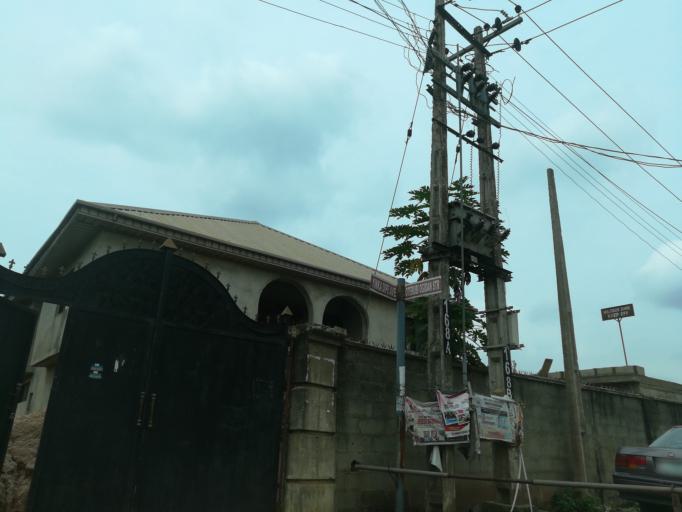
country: NG
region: Lagos
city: Ojota
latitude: 6.6052
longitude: 3.4152
